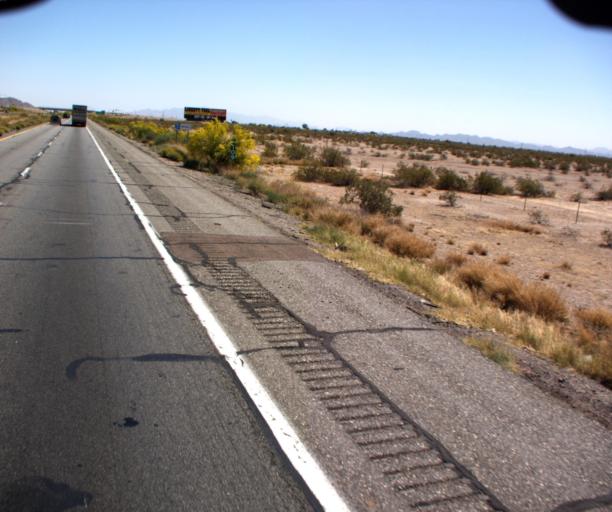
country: US
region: Arizona
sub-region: Maricopa County
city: Buckeye
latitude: 33.4417
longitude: -112.6891
